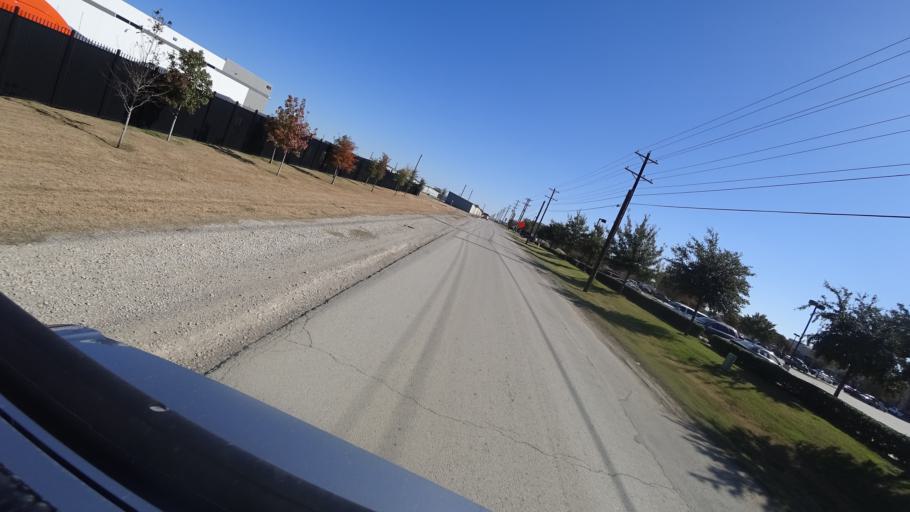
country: US
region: Texas
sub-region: Denton County
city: Lewisville
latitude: 33.0468
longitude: -96.9395
